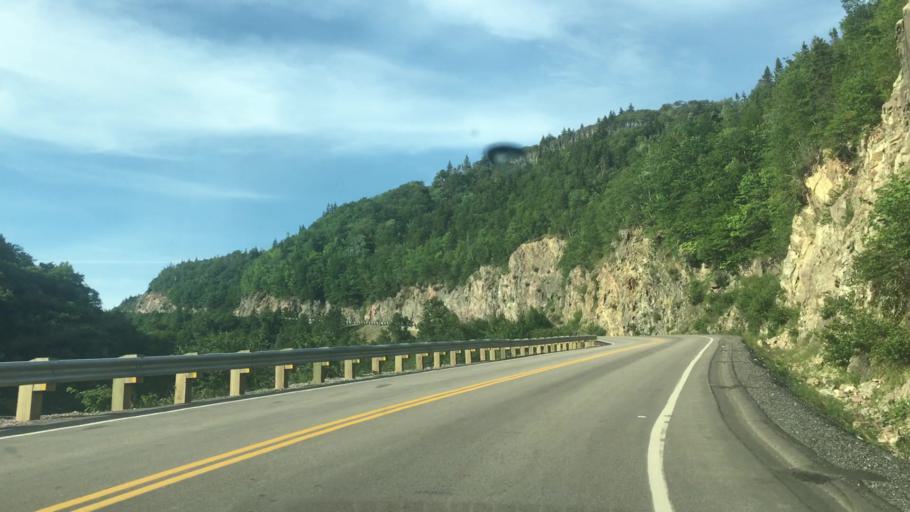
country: CA
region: Nova Scotia
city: Sydney Mines
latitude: 46.8154
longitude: -60.6515
